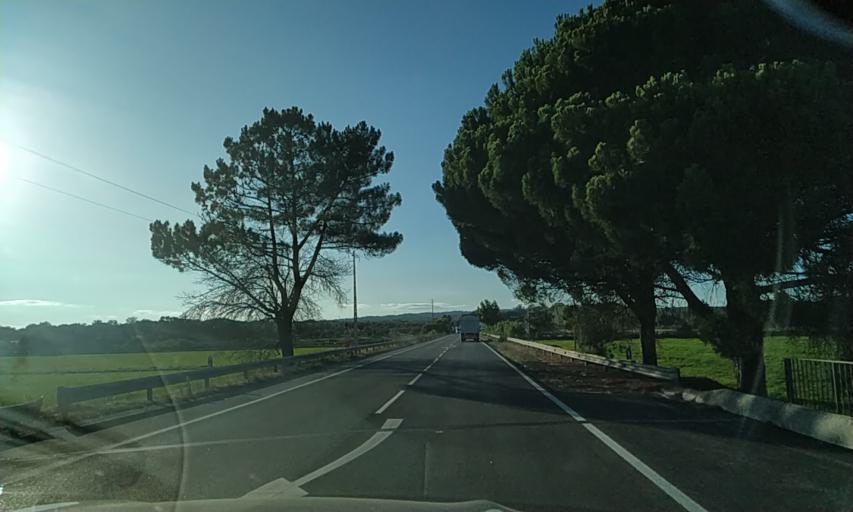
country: PT
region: Setubal
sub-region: Alcacer do Sal
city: Alcacer do Sal
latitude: 38.4705
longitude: -8.5864
